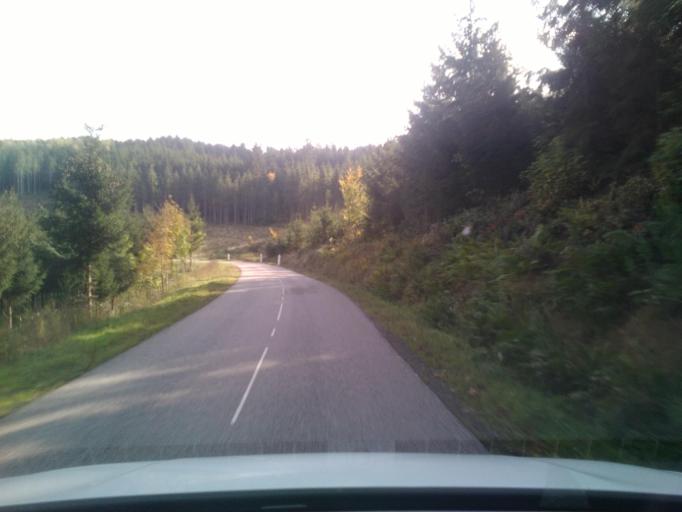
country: FR
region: Lorraine
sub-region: Departement des Vosges
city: Senones
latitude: 48.3786
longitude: 7.0543
